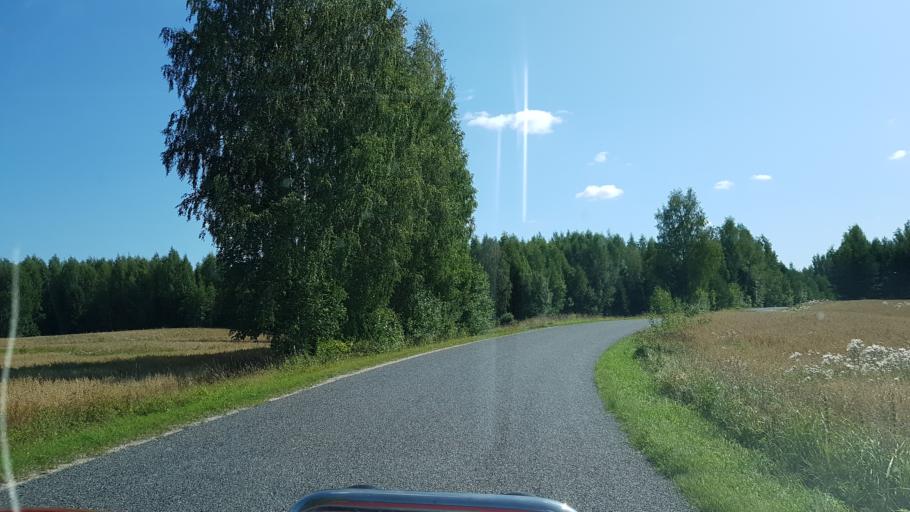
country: RU
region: Pskov
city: Pechory
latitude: 57.7594
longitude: 27.3294
